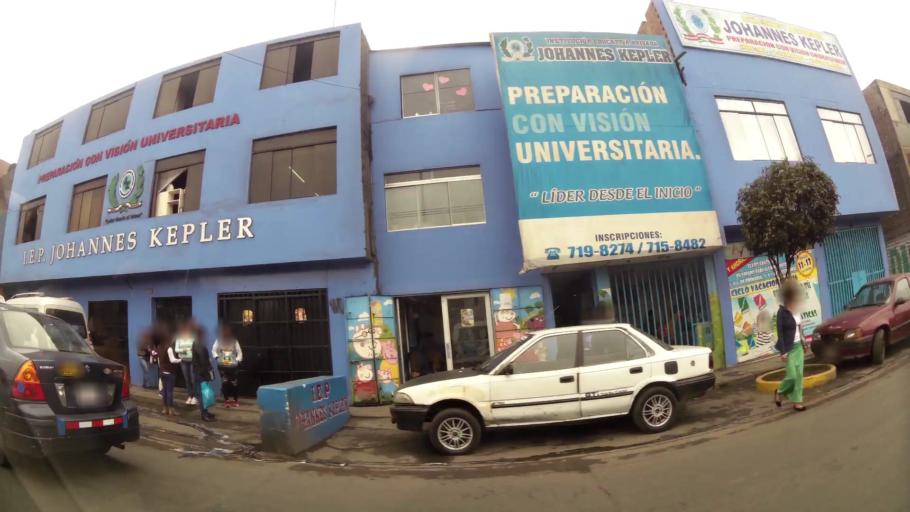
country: PE
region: Lima
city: Lima
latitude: -12.0456
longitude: -76.9988
